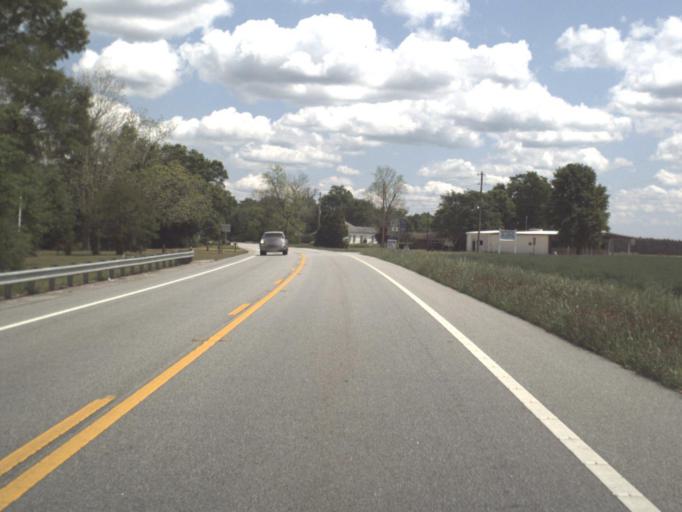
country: US
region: Alabama
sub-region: Escambia County
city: Atmore
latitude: 30.8897
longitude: -87.4640
